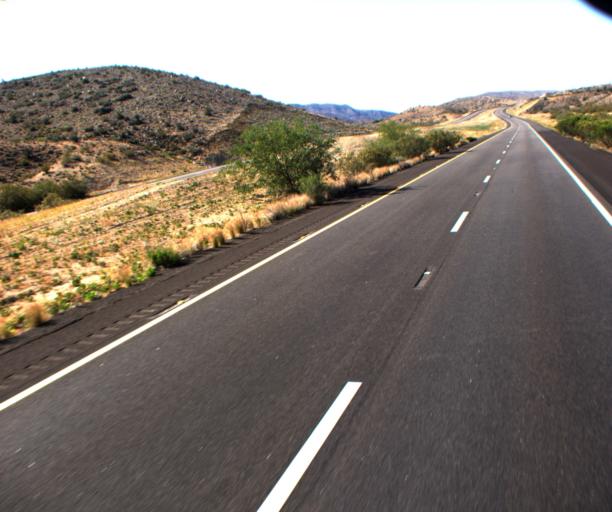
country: US
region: Arizona
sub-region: Mohave County
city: Kingman
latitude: 35.0221
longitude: -113.6648
